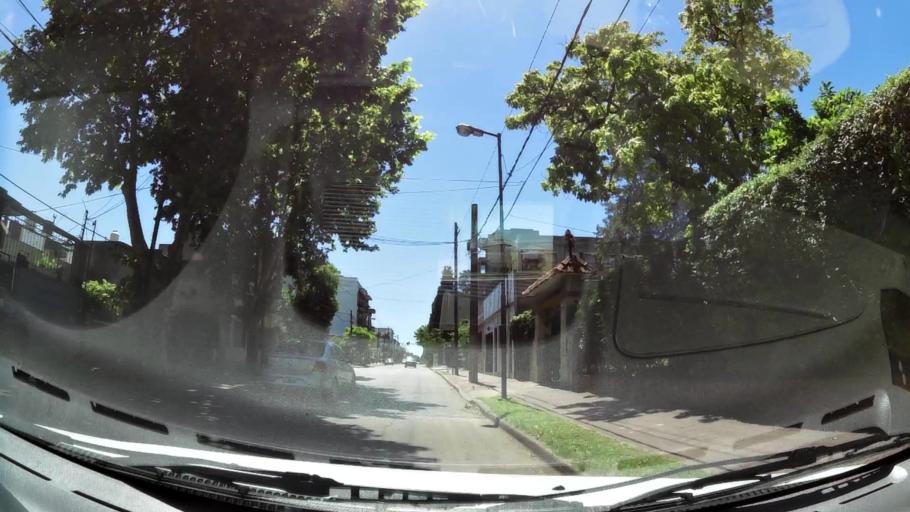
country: AR
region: Buenos Aires
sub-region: Partido de General San Martin
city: General San Martin
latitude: -34.5598
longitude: -58.5382
